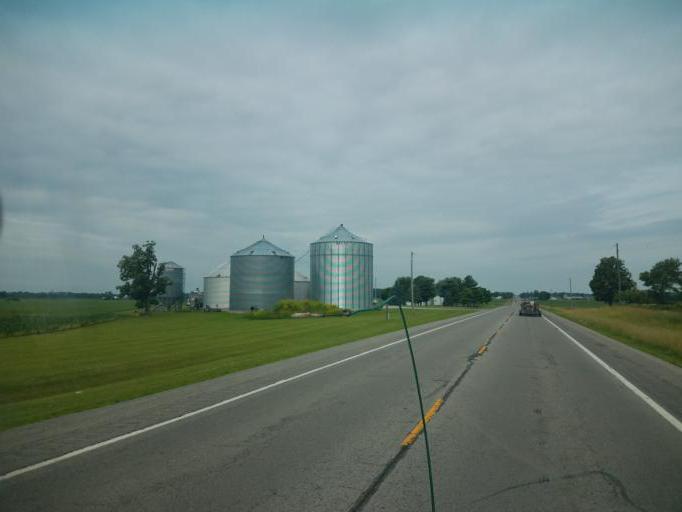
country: US
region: Ohio
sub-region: Hardin County
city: Kenton
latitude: 40.6930
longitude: -83.7004
